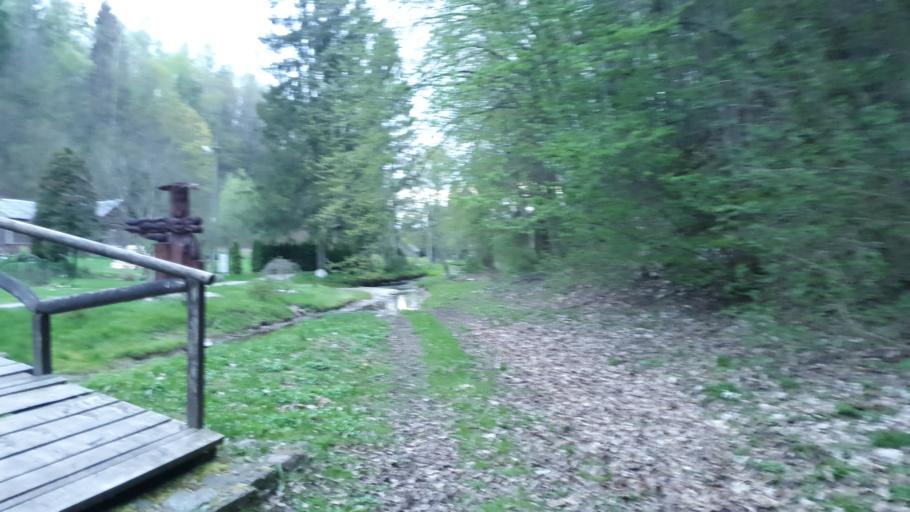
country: LT
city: Sakiai
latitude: 55.0799
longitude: 23.1786
